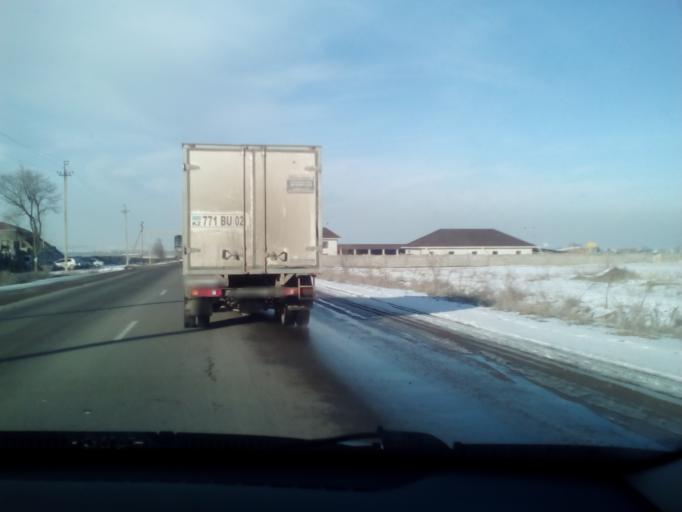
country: KZ
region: Almaty Oblysy
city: Burunday
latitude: 43.2020
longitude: 76.4149
